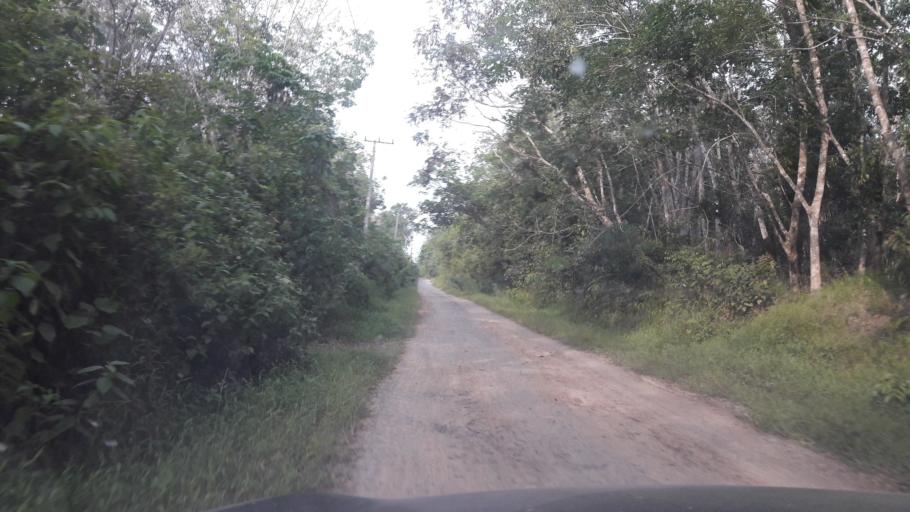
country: ID
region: South Sumatra
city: Gunungmenang
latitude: -3.2451
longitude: 104.0023
